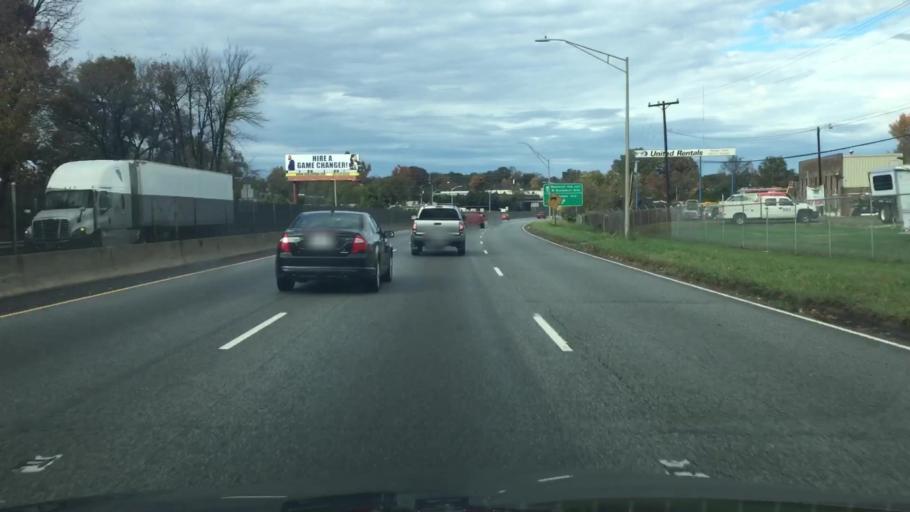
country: US
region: North Carolina
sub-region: Guilford County
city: Greensboro
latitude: 36.0818
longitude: -79.7673
